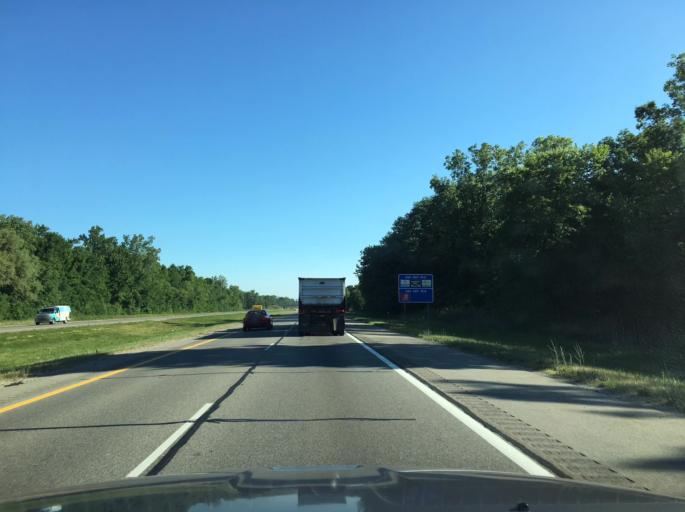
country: US
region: Michigan
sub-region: Macomb County
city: Shelby
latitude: 42.6616
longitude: -83.0143
